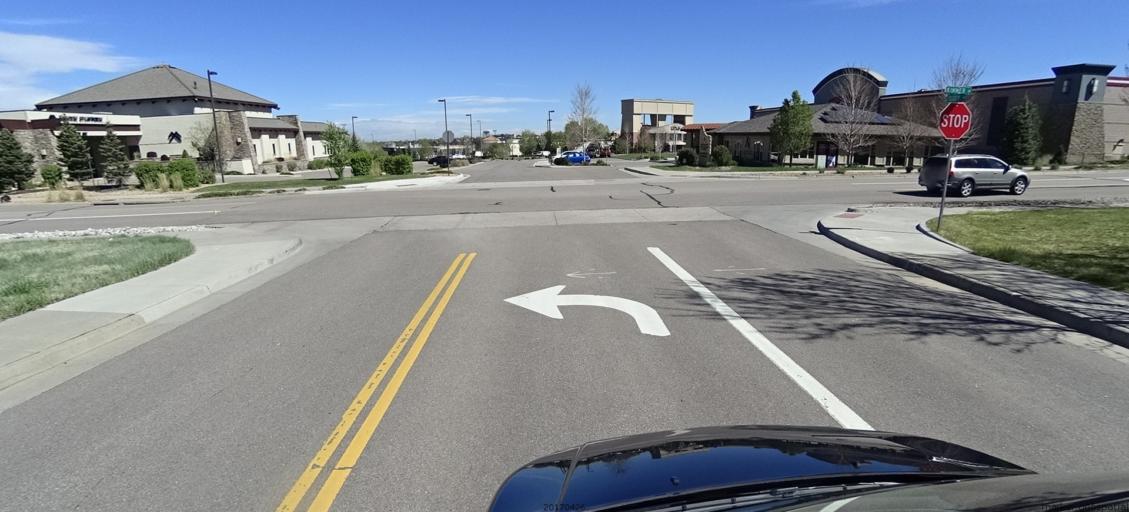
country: US
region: Colorado
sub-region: Adams County
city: Lone Tree
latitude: 39.5524
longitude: -104.8832
